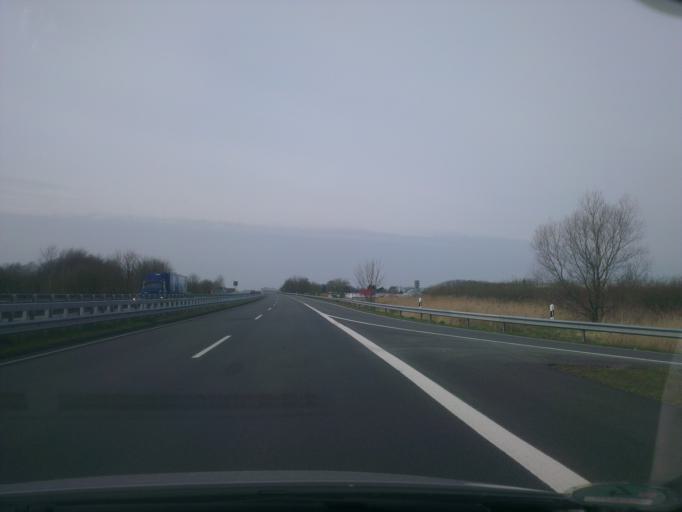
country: DE
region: Lower Saxony
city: Emden
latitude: 53.3881
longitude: 7.2156
